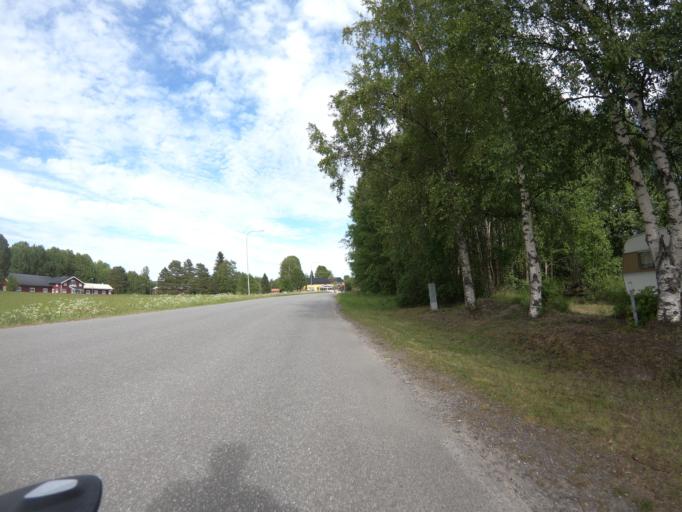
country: SE
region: Vaesterbotten
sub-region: Umea Kommun
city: Umea
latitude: 63.8034
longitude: 20.3054
